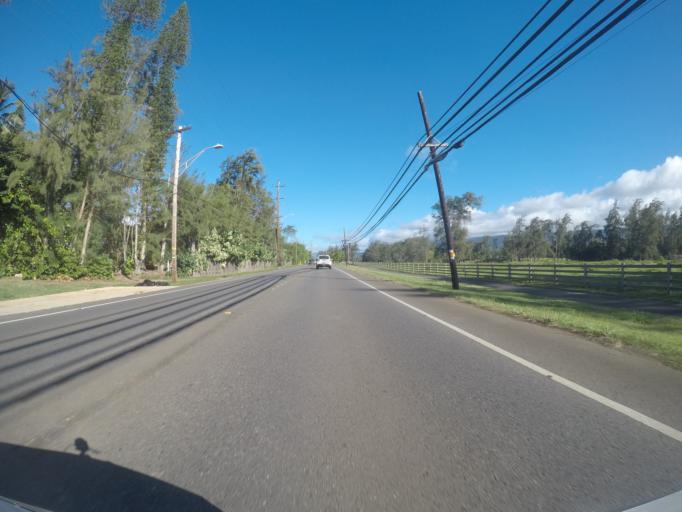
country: US
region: Hawaii
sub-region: Honolulu County
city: Kahuku
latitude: 21.6665
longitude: -157.9376
